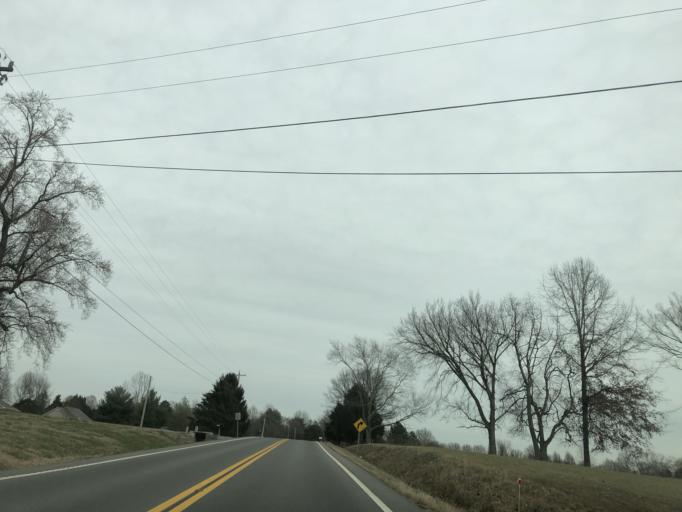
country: US
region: Tennessee
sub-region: Robertson County
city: Greenbrier
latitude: 36.4810
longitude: -86.7840
